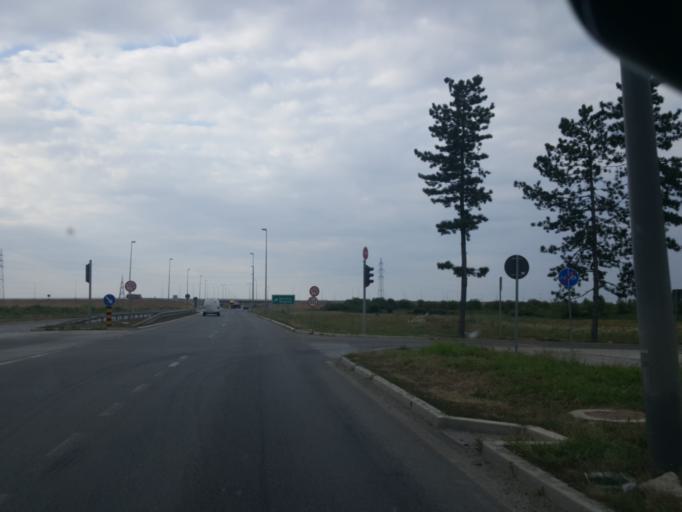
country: RS
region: Autonomna Pokrajina Vojvodina
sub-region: Juznobacki Okrug
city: Novi Sad
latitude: 45.3012
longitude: 19.8081
